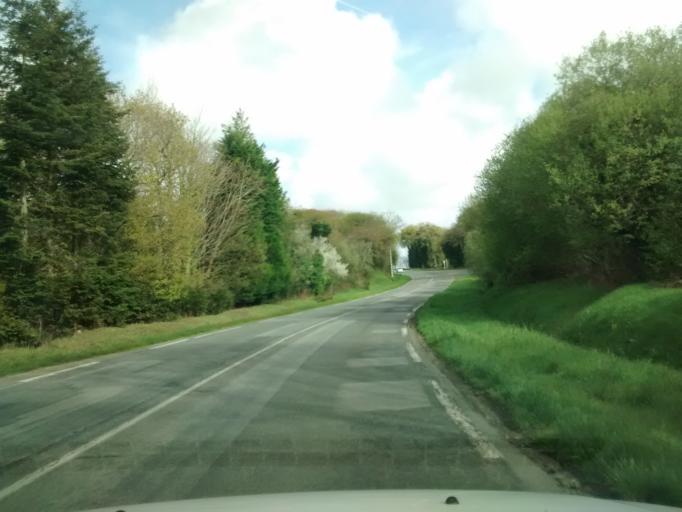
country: FR
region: Brittany
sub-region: Departement du Morbihan
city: Queven
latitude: 47.7780
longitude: -3.4265
